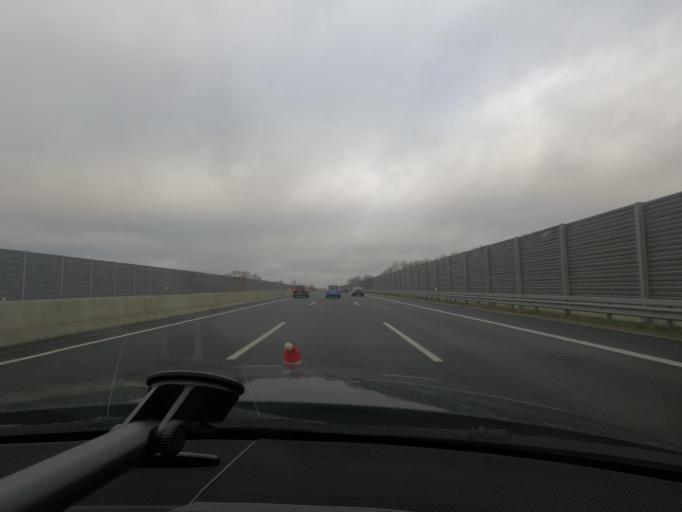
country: DE
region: Schleswig-Holstein
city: Ellerau
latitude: 53.7553
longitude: 9.9500
